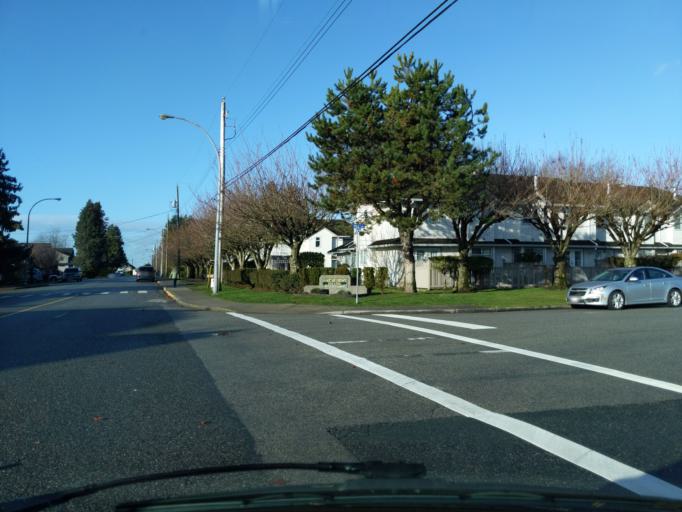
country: CA
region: British Columbia
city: Pitt Meadows
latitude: 49.2190
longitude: -122.6934
